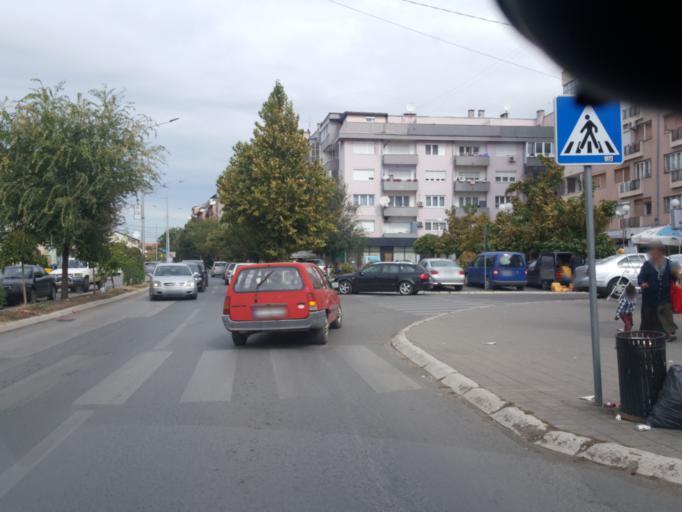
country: XK
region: Gjakova
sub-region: Komuna e Gjakoves
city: Gjakove
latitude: 42.3862
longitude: 20.4280
